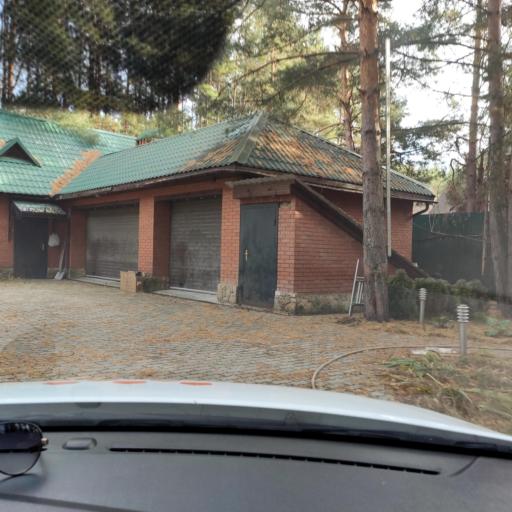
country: RU
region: Tatarstan
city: Verkhniy Uslon
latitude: 55.6206
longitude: 49.0210
